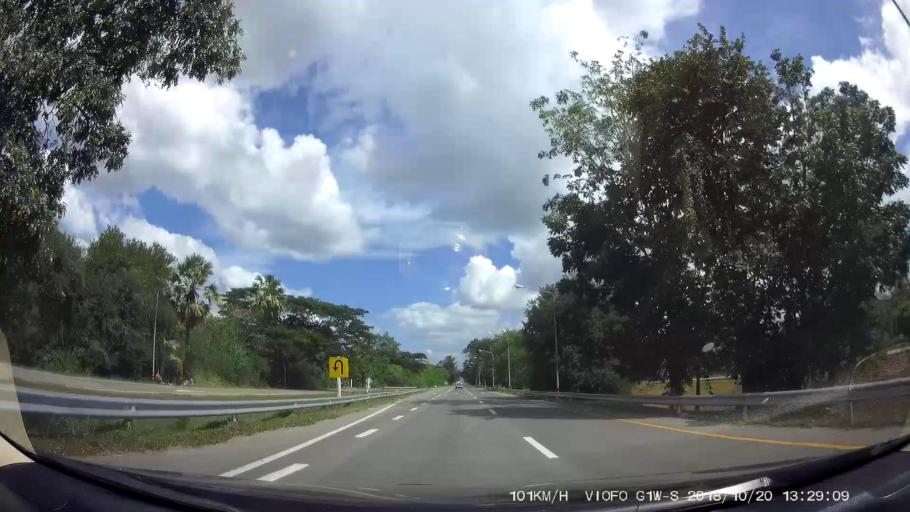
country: TH
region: Chaiyaphum
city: Khon San
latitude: 16.5905
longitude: 101.9858
